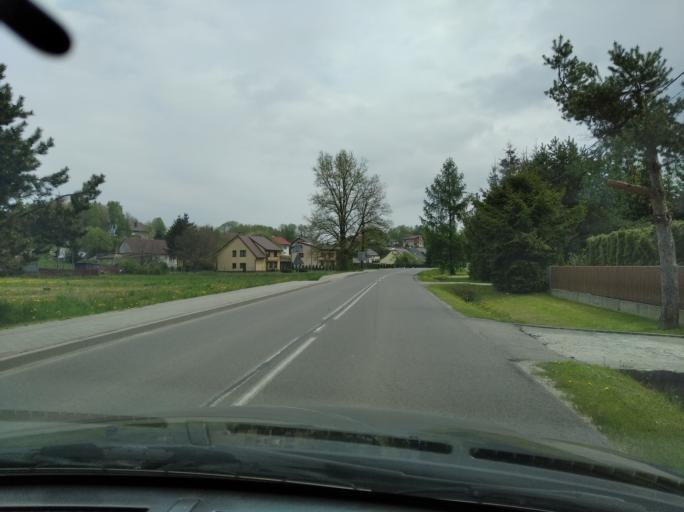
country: PL
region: Lesser Poland Voivodeship
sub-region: Powiat tarnowski
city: Szynwald
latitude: 49.9875
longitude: 21.0984
